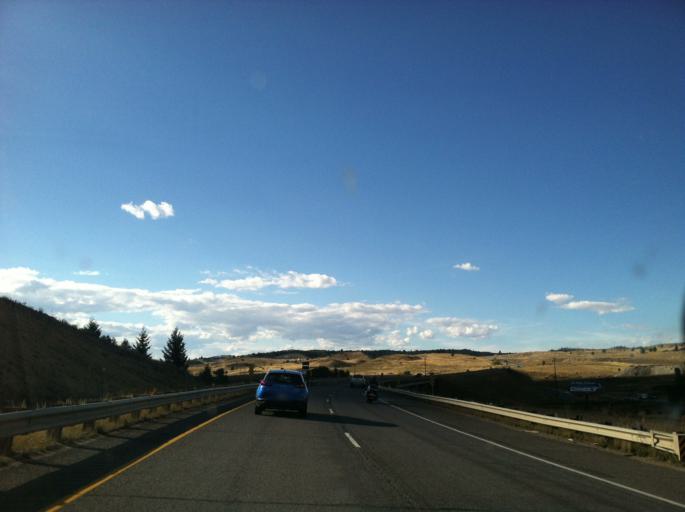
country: US
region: Montana
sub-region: Silver Bow County
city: Butte
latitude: 45.9958
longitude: -112.5628
